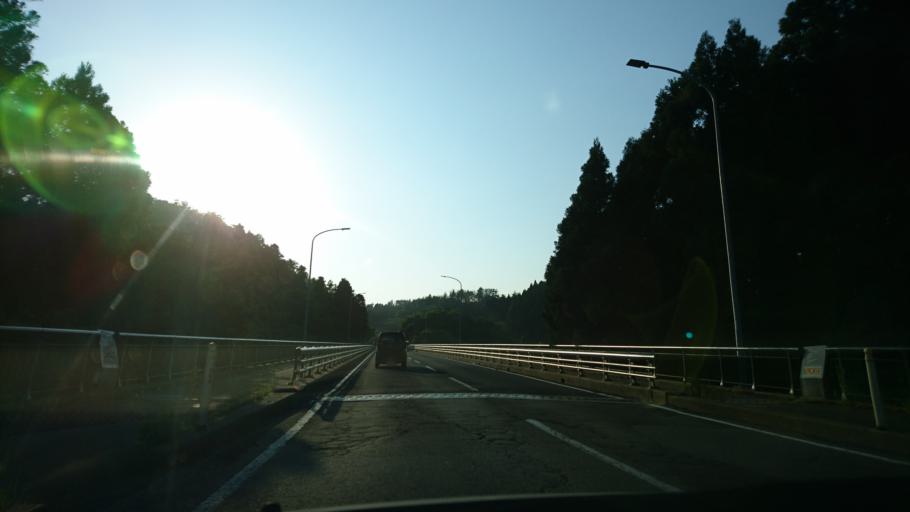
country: JP
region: Iwate
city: Ofunato
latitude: 38.9146
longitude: 141.5248
